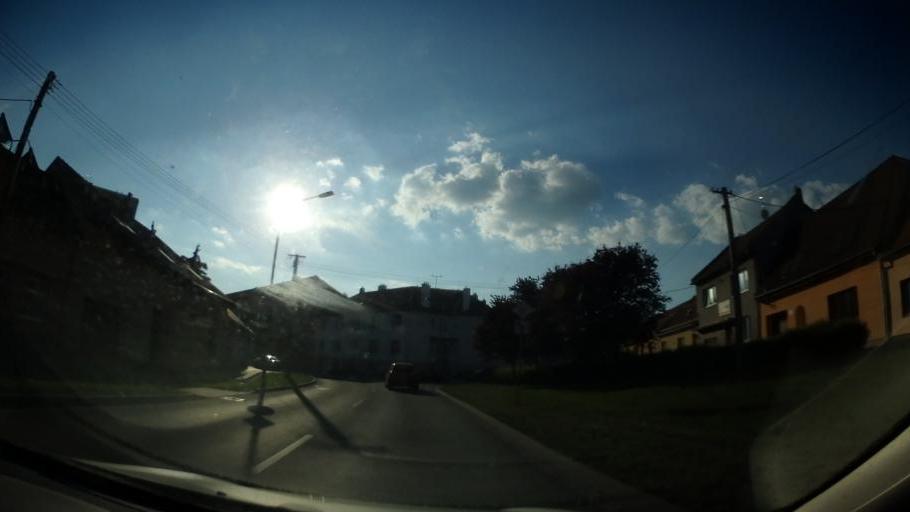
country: CZ
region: South Moravian
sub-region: Okres Vyskov
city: Vyskov
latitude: 49.2806
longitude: 17.0058
